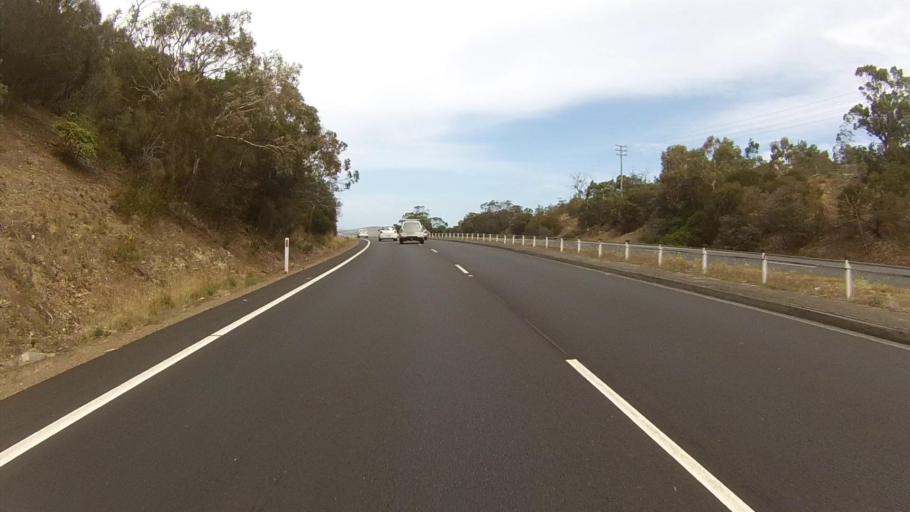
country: AU
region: Tasmania
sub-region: Clarence
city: Warrane
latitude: -42.8644
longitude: 147.3933
